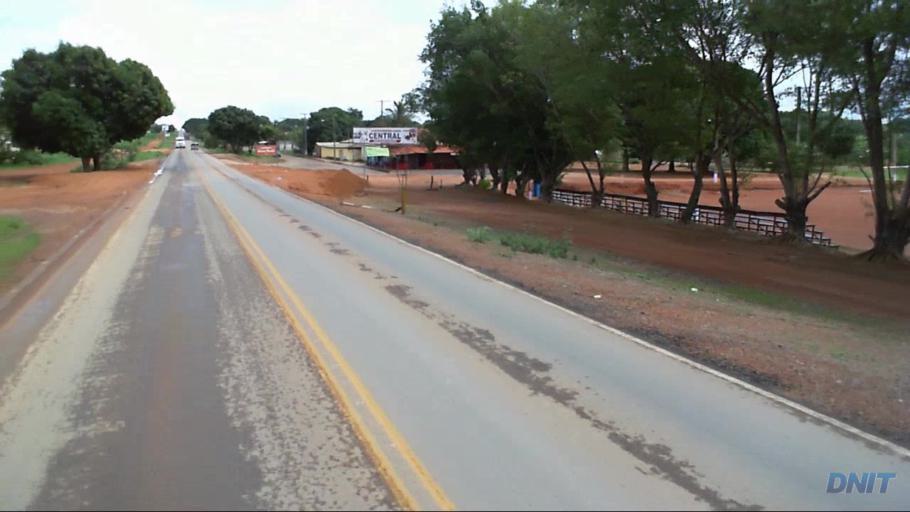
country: BR
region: Goias
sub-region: Padre Bernardo
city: Padre Bernardo
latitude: -15.2636
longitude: -48.2647
